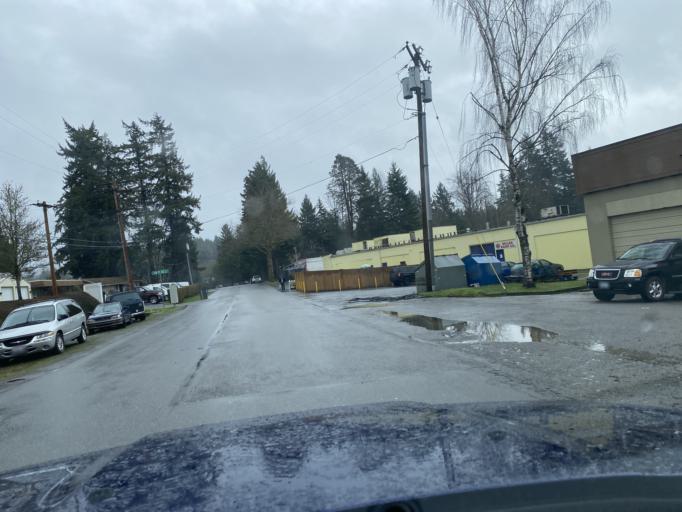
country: US
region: Washington
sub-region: King County
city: Bellevue
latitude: 47.6244
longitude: -122.1578
